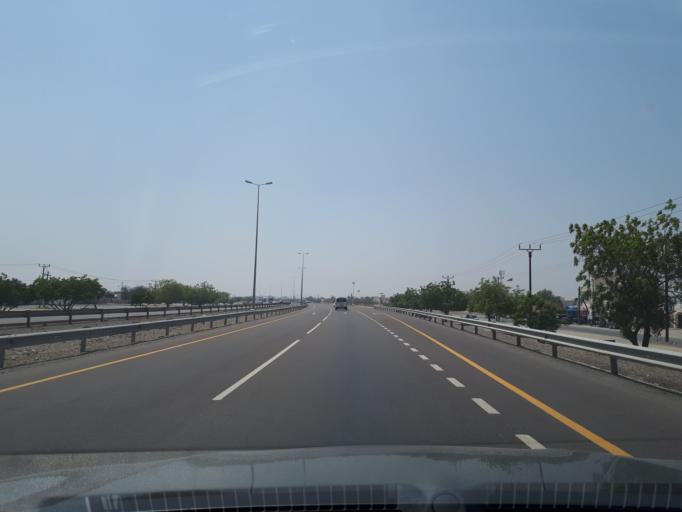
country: OM
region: Al Batinah
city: Al Liwa'
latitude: 24.4753
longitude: 56.5955
